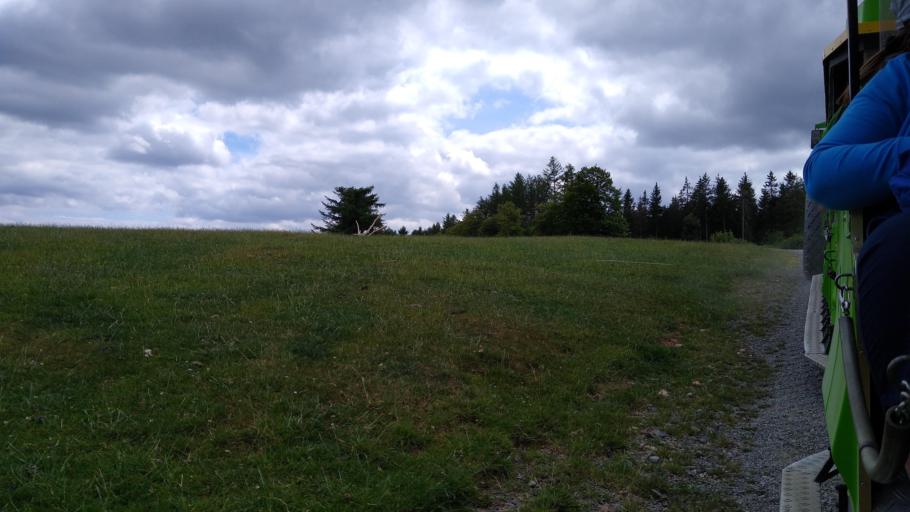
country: DE
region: North Rhine-Westphalia
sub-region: Regierungsbezirk Arnsberg
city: Kirchhundem
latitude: 51.0634
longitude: 8.1787
